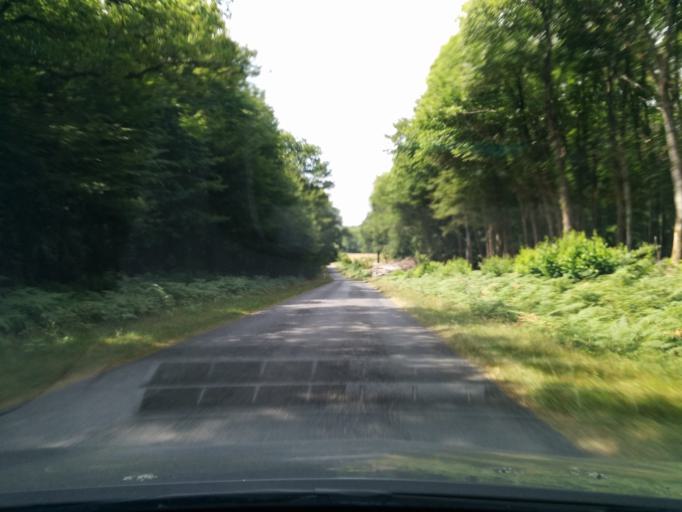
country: FR
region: Centre
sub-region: Departement du Cher
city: Henrichemont
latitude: 47.3502
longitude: 2.6211
